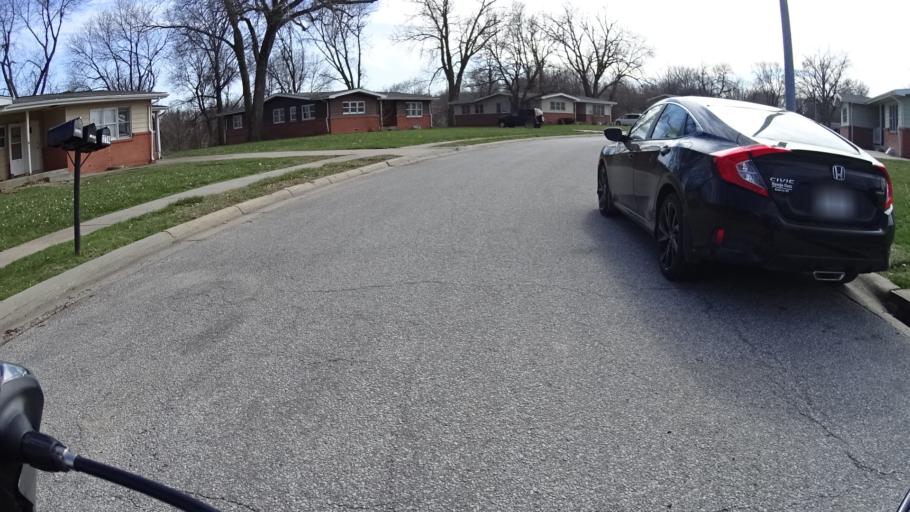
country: US
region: Nebraska
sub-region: Sarpy County
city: Offutt Air Force Base
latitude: 41.1189
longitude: -95.9585
